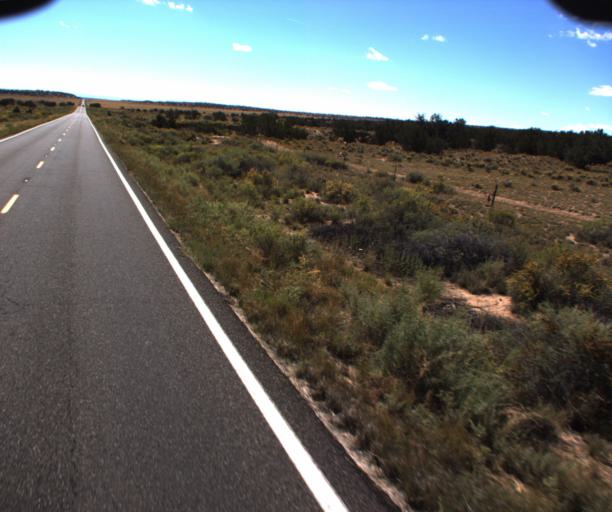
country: US
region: Arizona
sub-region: Apache County
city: Saint Johns
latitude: 34.7794
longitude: -109.2388
